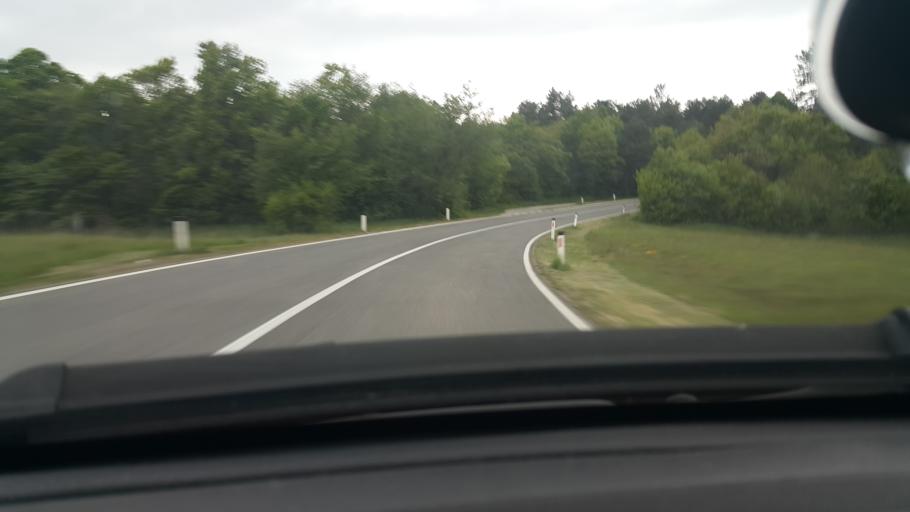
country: SI
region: Divaca
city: Divaca
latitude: 45.6899
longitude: 13.9631
